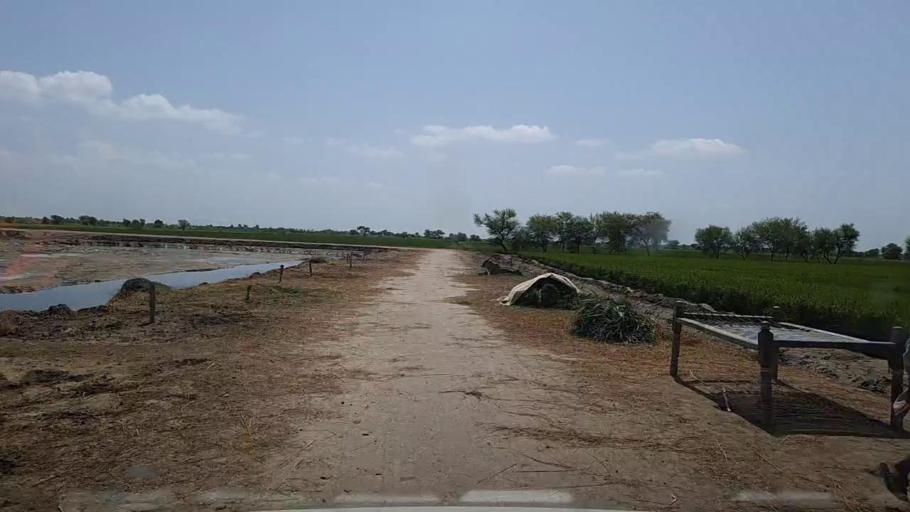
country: PK
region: Sindh
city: Kario
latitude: 24.6851
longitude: 68.5940
